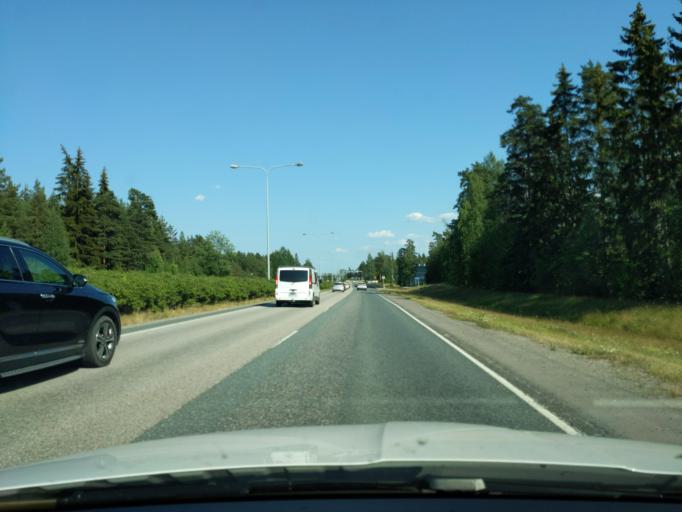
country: FI
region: Paijanne Tavastia
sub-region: Lahti
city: Lahti
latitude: 60.9802
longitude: 25.6013
